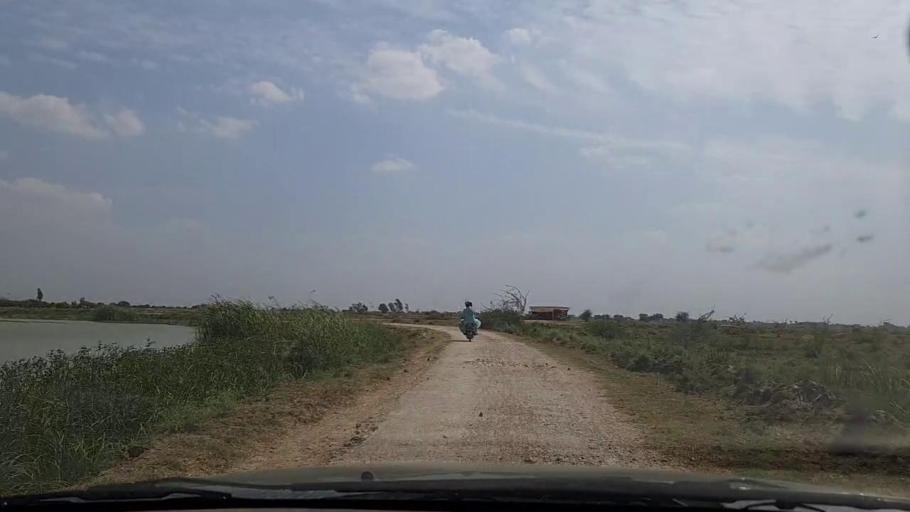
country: PK
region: Sindh
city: Mirpur Batoro
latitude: 24.5479
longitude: 68.2555
